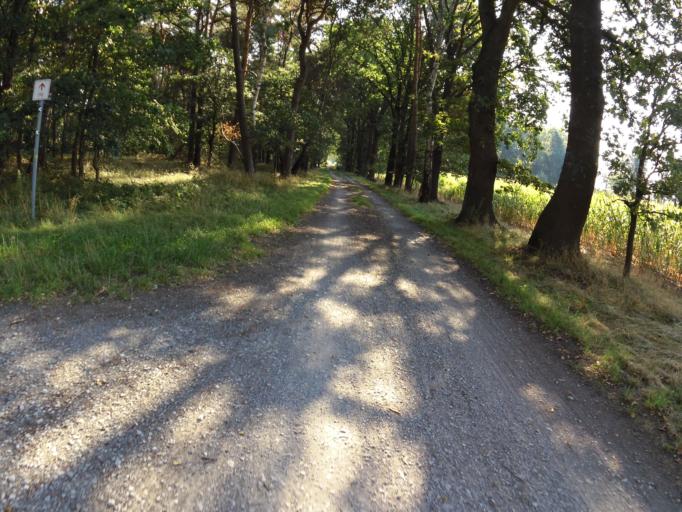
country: DE
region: North Rhine-Westphalia
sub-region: Regierungsbezirk Munster
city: Beelen
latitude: 51.9531
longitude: 8.1435
